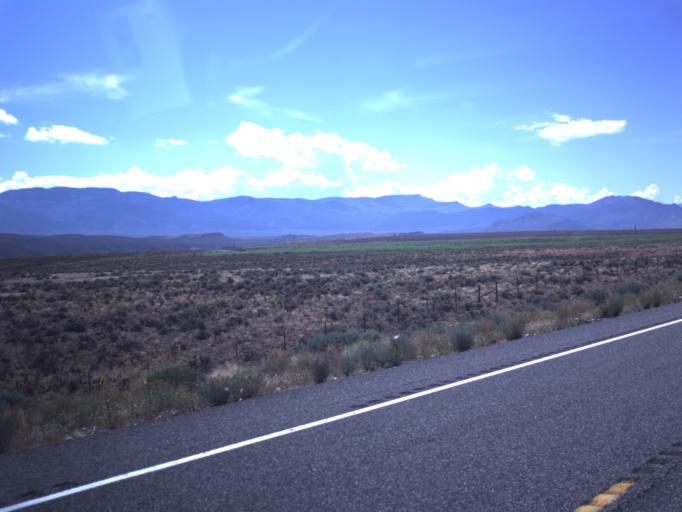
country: US
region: Utah
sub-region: Piute County
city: Junction
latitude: 38.4263
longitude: -112.2317
